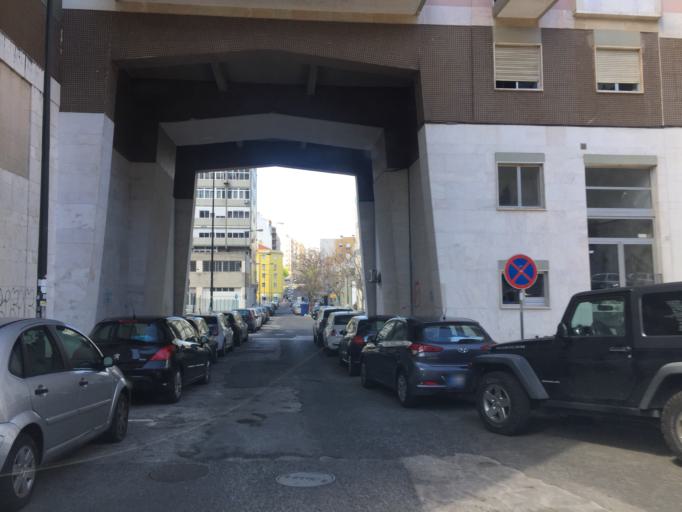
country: PT
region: Lisbon
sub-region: Odivelas
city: Olival do Basto
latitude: 38.7686
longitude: -9.1561
